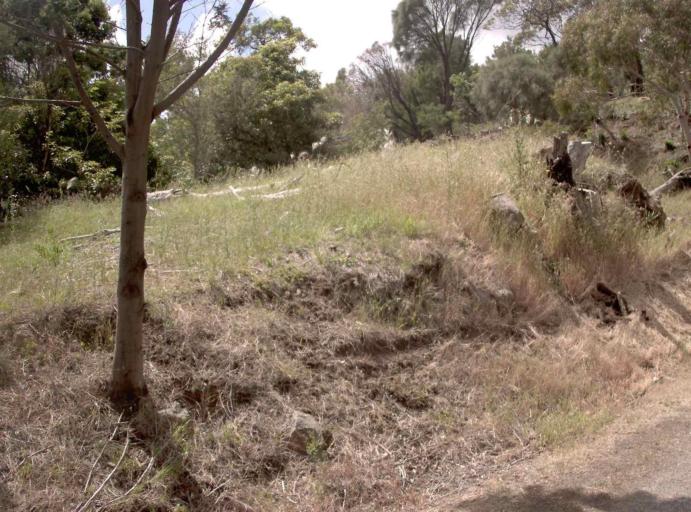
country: AU
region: Victoria
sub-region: Mornington Peninsula
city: Dromana
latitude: -38.3489
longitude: 144.9504
